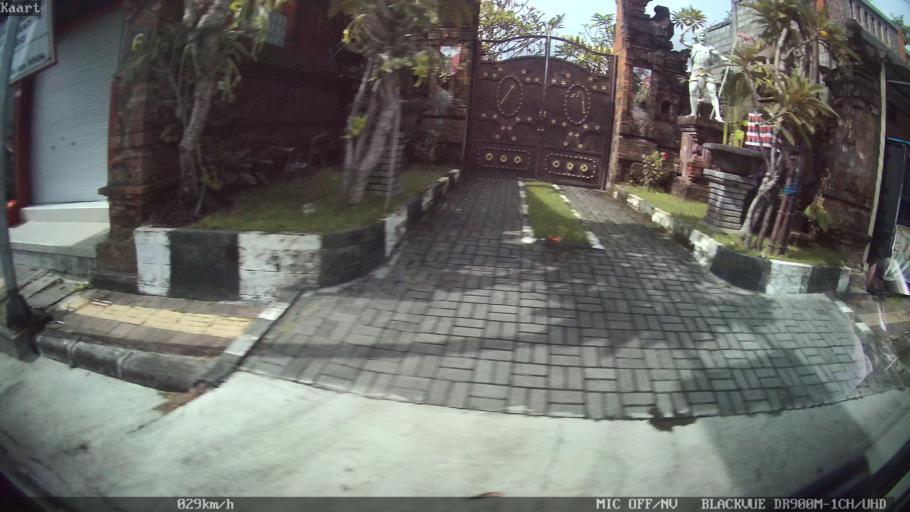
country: ID
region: Bali
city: Banjar Kertasari
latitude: -8.6201
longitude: 115.2034
